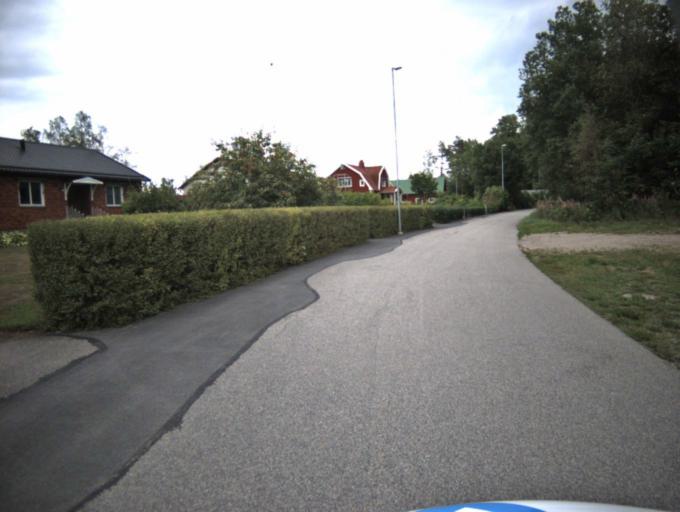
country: SE
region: Vaestra Goetaland
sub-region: Boras Kommun
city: Dalsjofors
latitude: 57.8306
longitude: 13.1970
